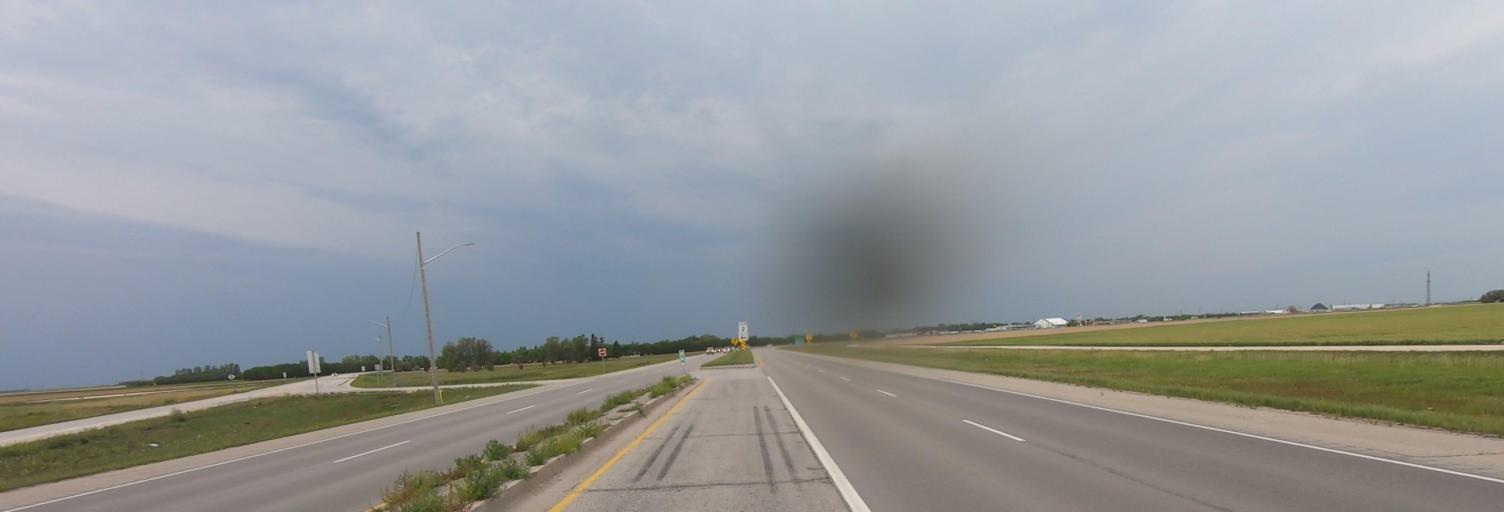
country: CA
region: Manitoba
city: Headingley
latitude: 49.7697
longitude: -97.3045
